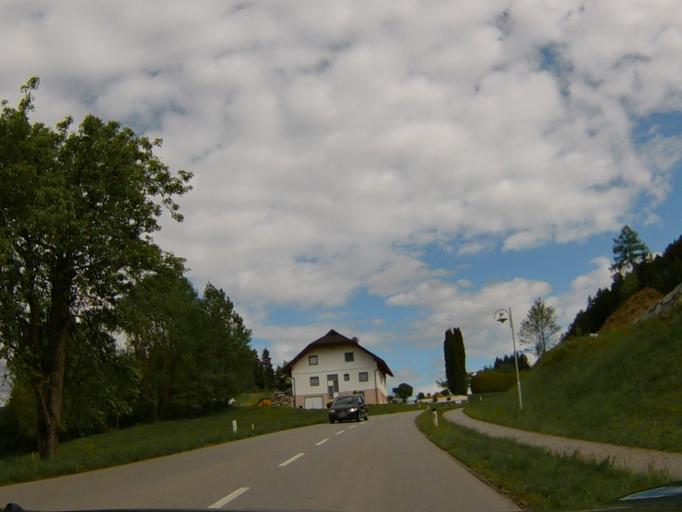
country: AT
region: Carinthia
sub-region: Politischer Bezirk Villach Land
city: Stockenboi
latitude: 46.7382
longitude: 13.5790
